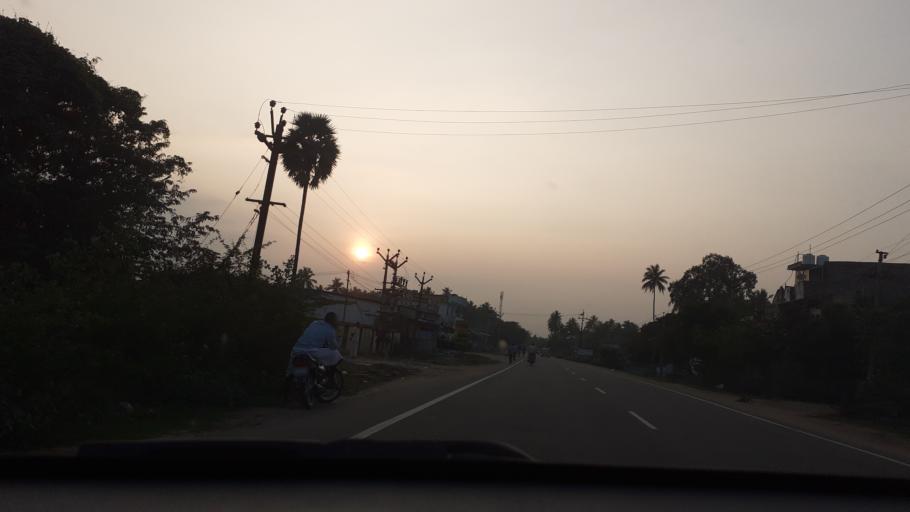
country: IN
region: Tamil Nadu
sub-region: Dindigul
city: Palani
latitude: 10.4326
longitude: 77.5214
